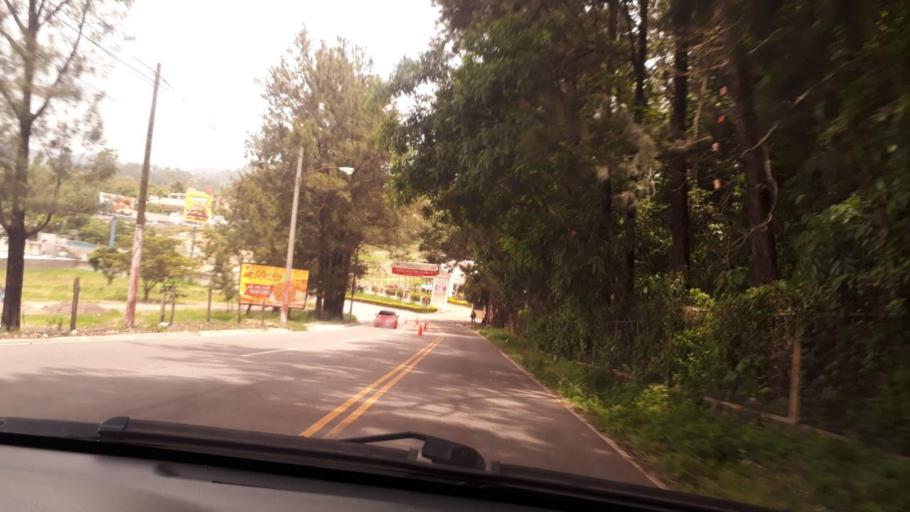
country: GT
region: Chiquimula
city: Esquipulas
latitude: 14.5629
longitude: -89.3596
